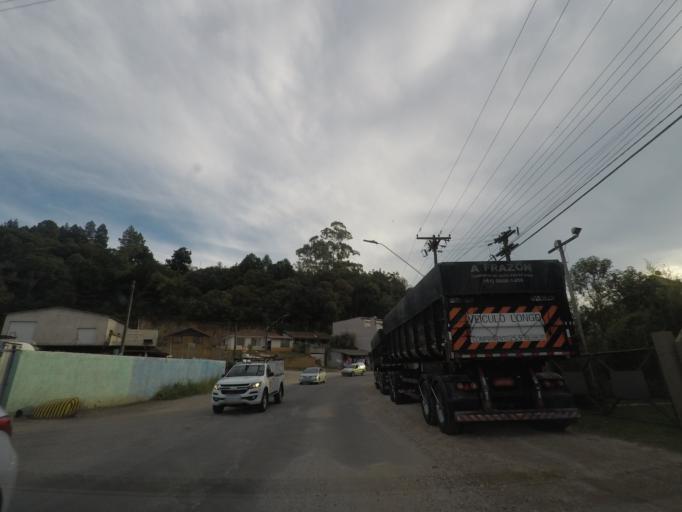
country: BR
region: Parana
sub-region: Colombo
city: Colombo
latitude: -25.2888
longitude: -49.2159
